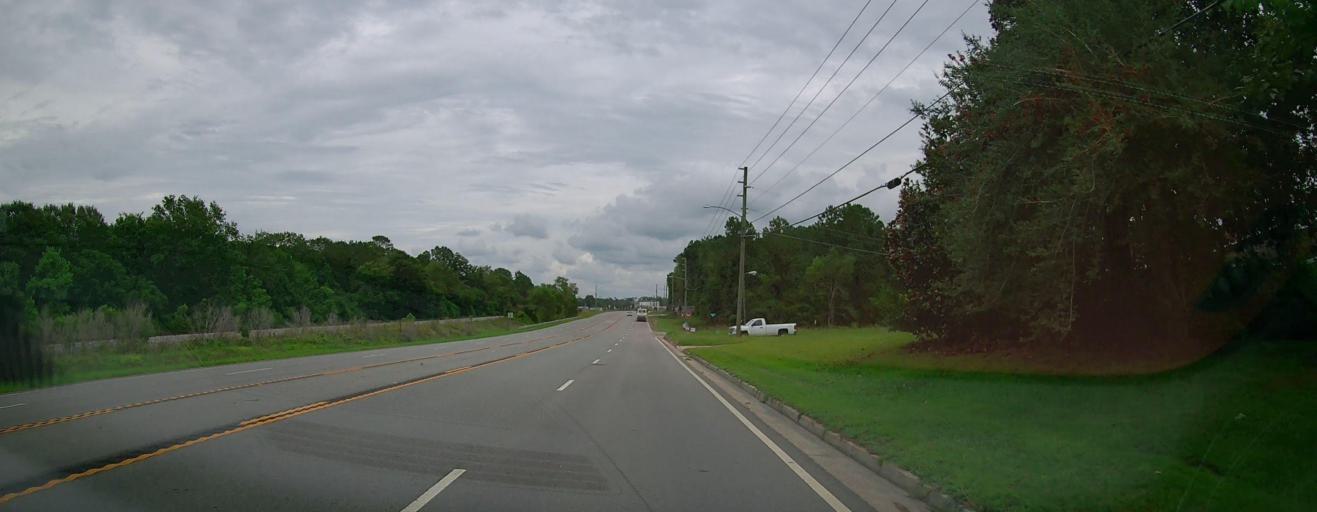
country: US
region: Georgia
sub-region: Telfair County
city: Helena
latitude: 32.0795
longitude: -82.9220
